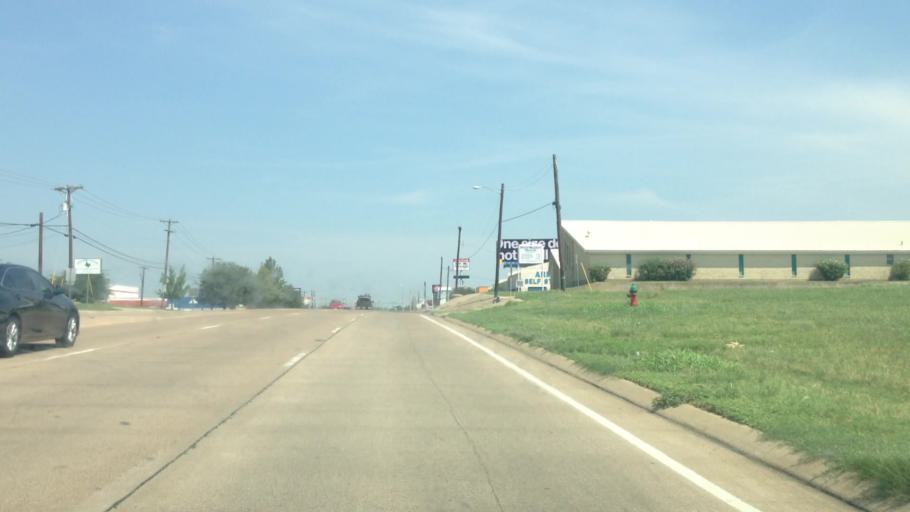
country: US
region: Texas
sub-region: Tarrant County
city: Watauga
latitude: 32.8510
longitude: -97.2639
